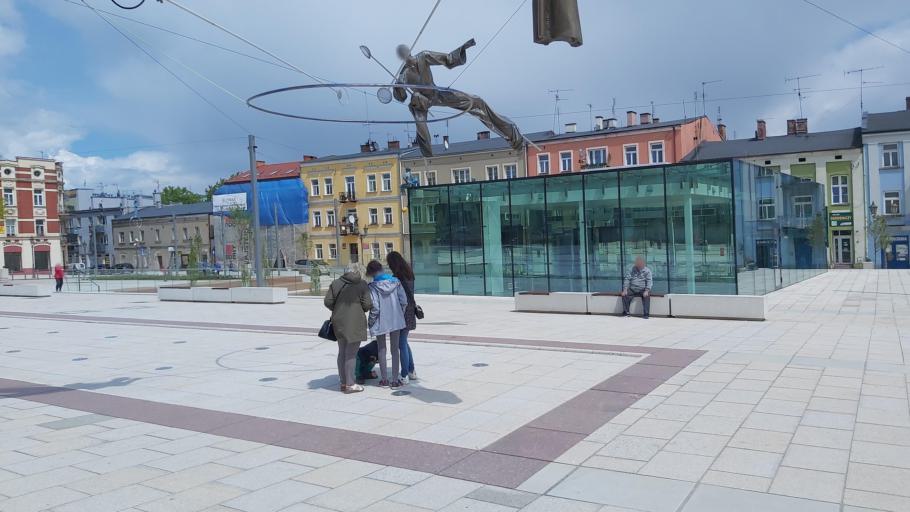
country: PL
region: Silesian Voivodeship
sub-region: Czestochowa
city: Czestochowa
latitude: 50.8120
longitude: 19.1290
